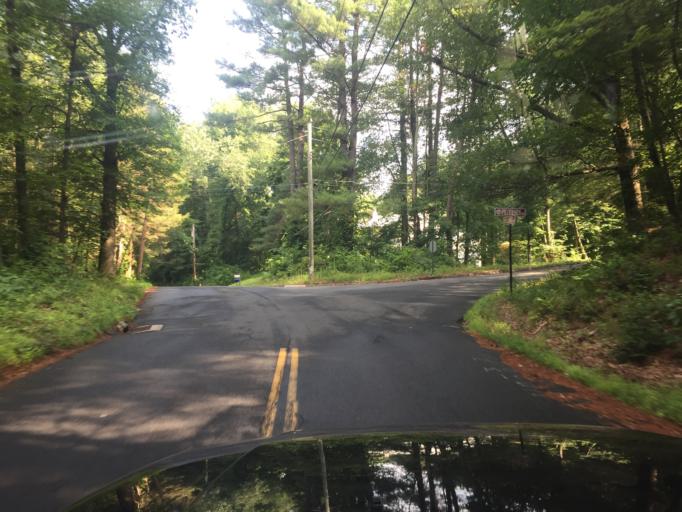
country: US
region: Connecticut
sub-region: Hartford County
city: Salmon Brook
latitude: 41.9561
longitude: -72.7796
